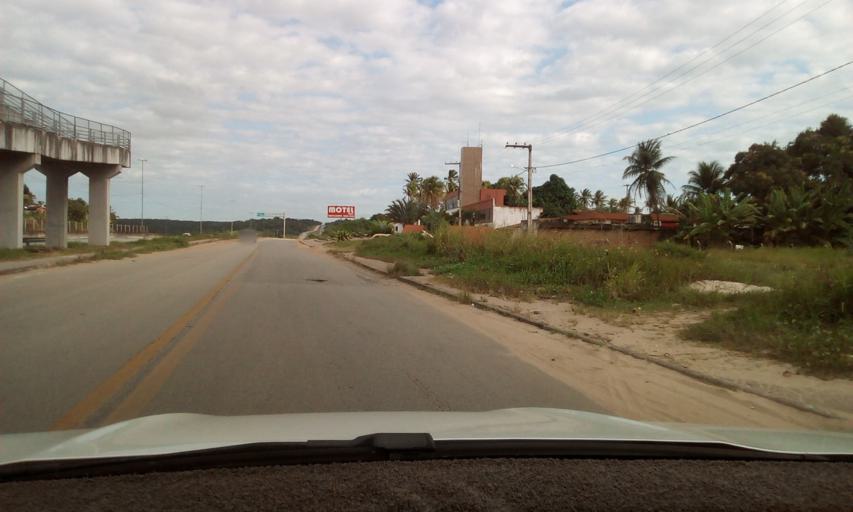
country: BR
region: Paraiba
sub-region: Mamanguape
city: Mamanguape
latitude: -6.8487
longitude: -35.1356
